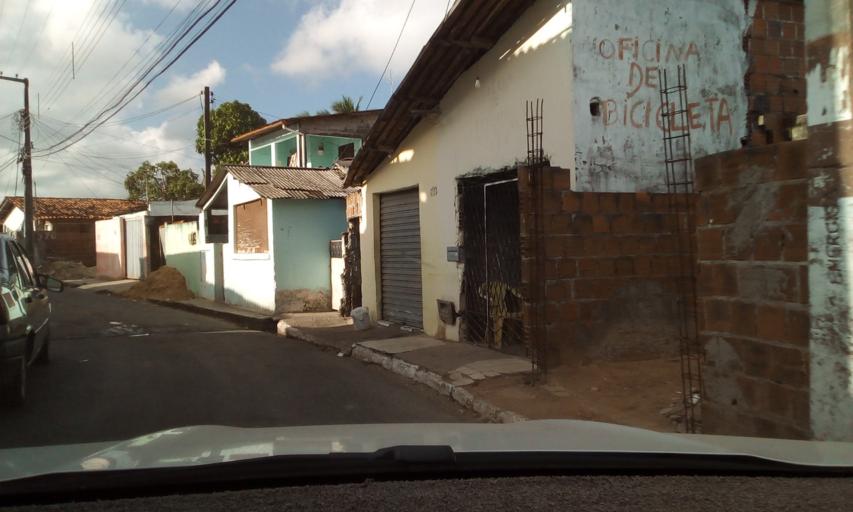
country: BR
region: Paraiba
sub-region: Joao Pessoa
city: Joao Pessoa
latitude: -7.0957
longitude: -34.8606
